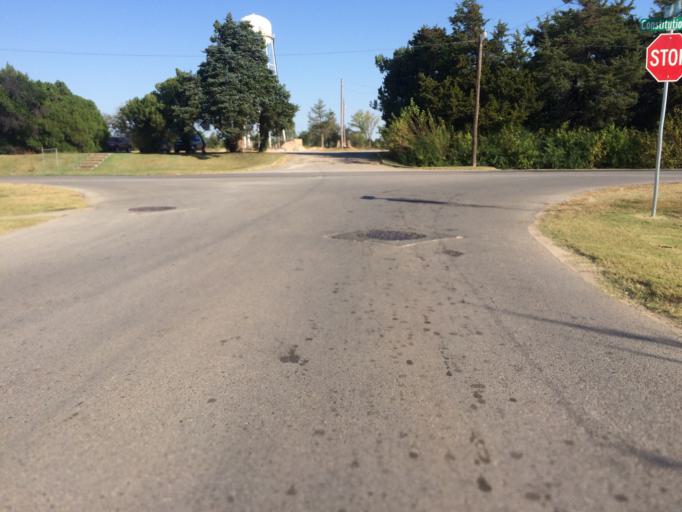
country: US
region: Oklahoma
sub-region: Cleveland County
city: Norman
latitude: 35.1910
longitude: -97.4322
